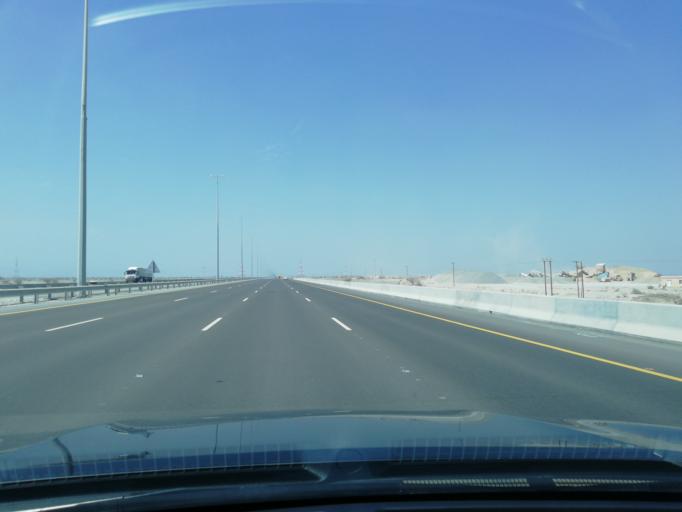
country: OM
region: Al Batinah
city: Barka'
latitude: 23.6222
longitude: 57.8426
